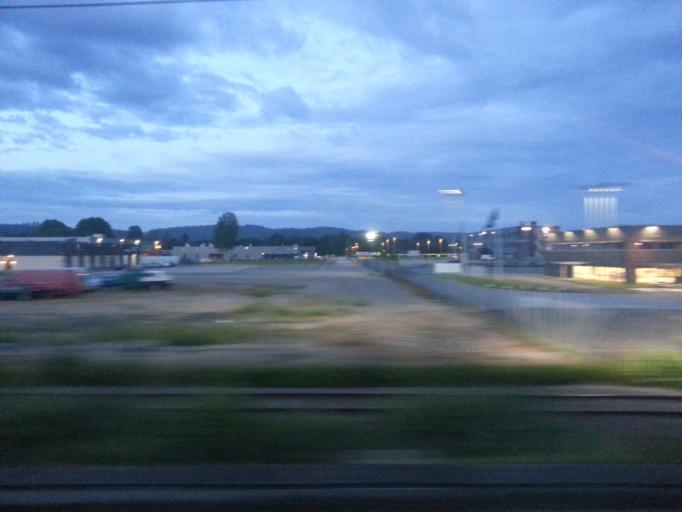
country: NO
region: Akershus
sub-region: Skedsmo
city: Lillestrom
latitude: 59.9683
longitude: 11.0680
